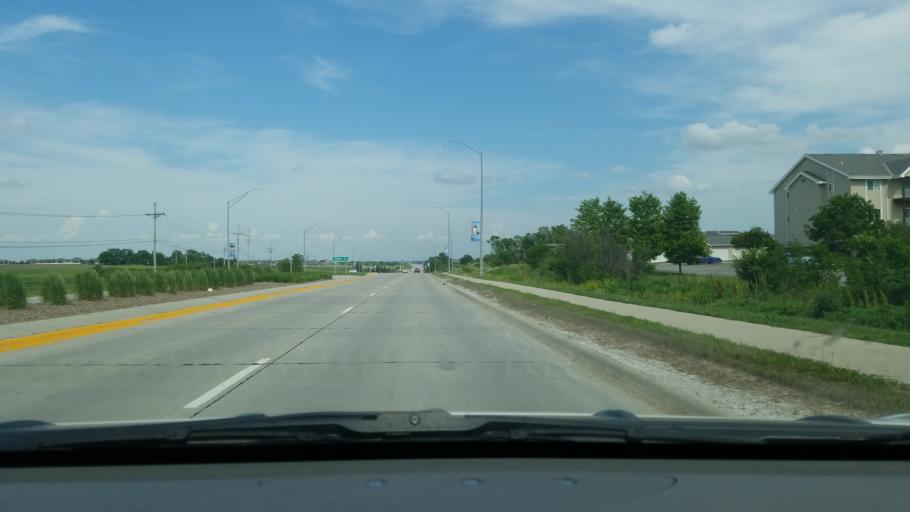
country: US
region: Nebraska
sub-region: Sarpy County
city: Gretna
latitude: 41.1469
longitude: -96.2315
